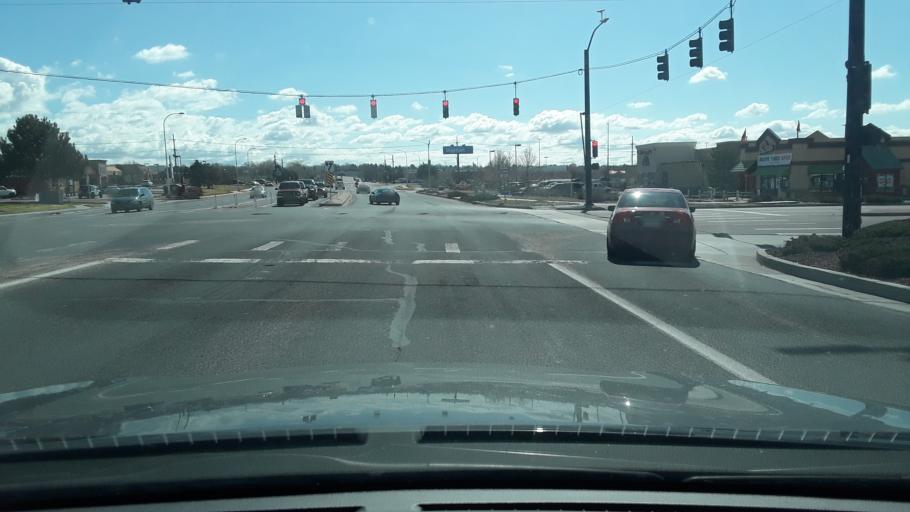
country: US
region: Colorado
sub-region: El Paso County
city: Cimarron Hills
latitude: 38.8571
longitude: -104.7234
